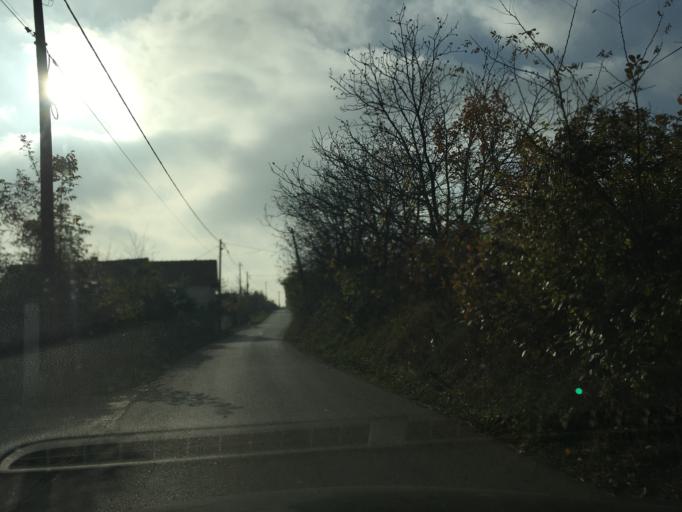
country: RS
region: Central Serbia
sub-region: Belgrade
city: Sopot
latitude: 44.4880
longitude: 20.5658
